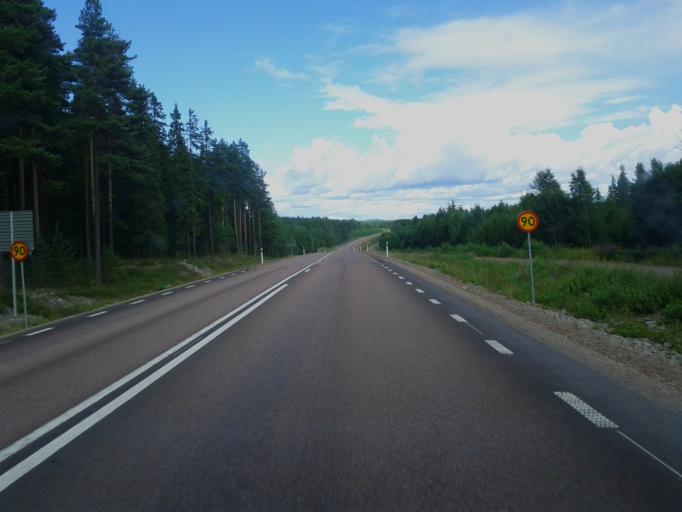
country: SE
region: Dalarna
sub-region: Rattviks Kommun
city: Raettvik
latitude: 60.8443
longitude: 15.1373
